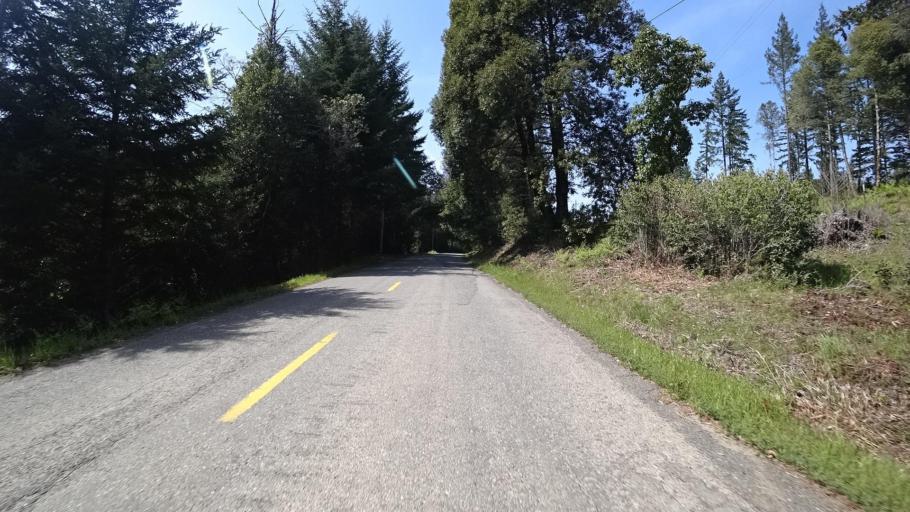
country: US
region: California
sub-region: Humboldt County
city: Redway
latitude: 40.3705
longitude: -123.7358
